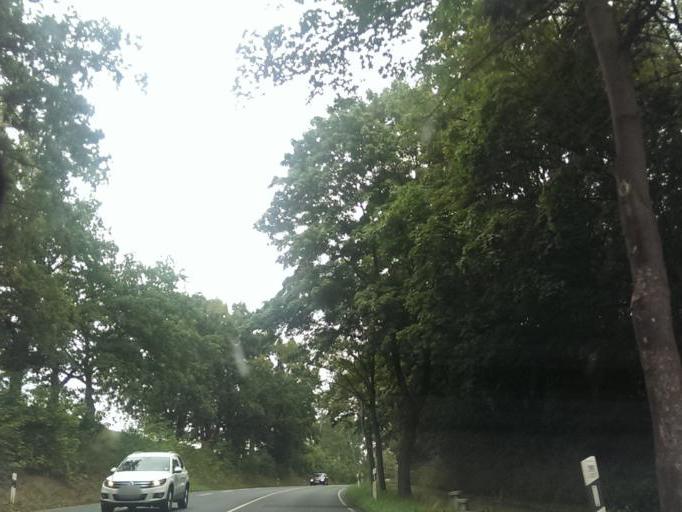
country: DE
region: Lower Saxony
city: Elze
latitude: 52.5519
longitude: 9.7237
